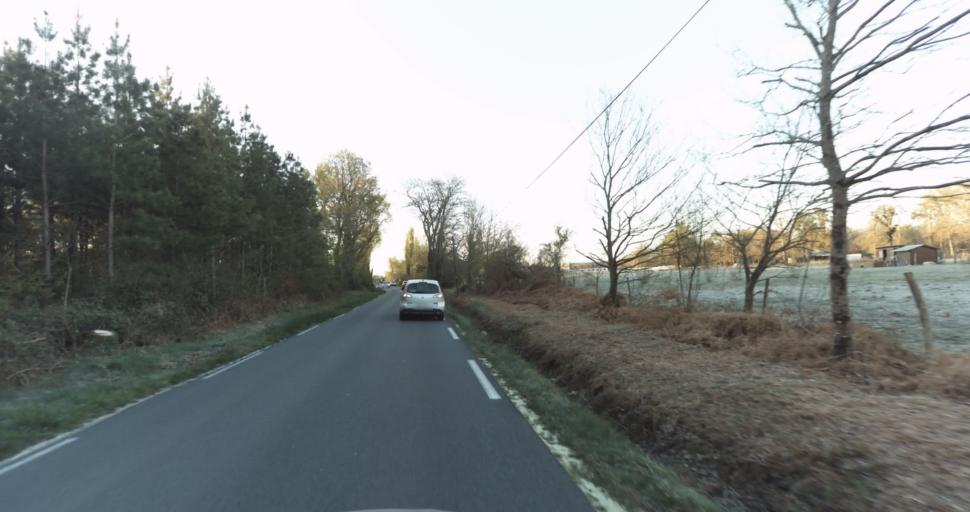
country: FR
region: Aquitaine
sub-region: Departement de la Gironde
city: Martignas-sur-Jalle
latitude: 44.8174
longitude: -0.7507
